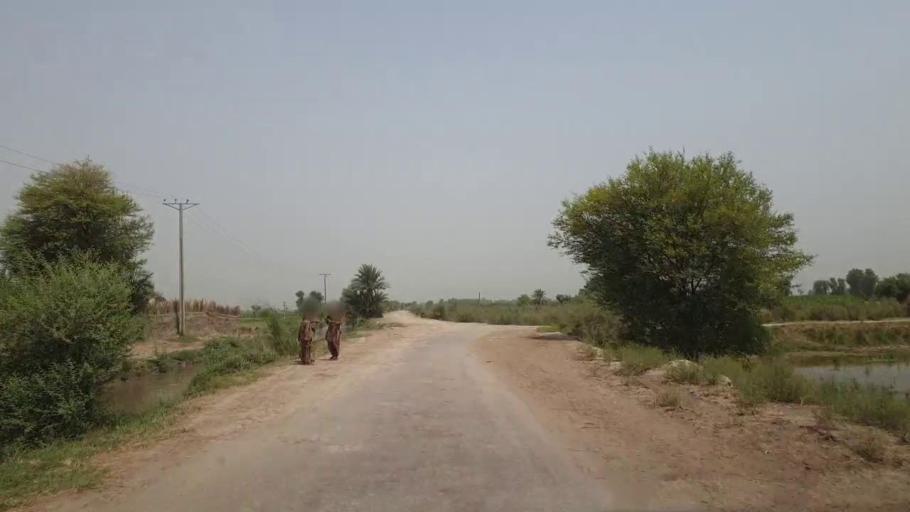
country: PK
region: Sindh
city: Gambat
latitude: 27.4461
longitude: 68.4448
